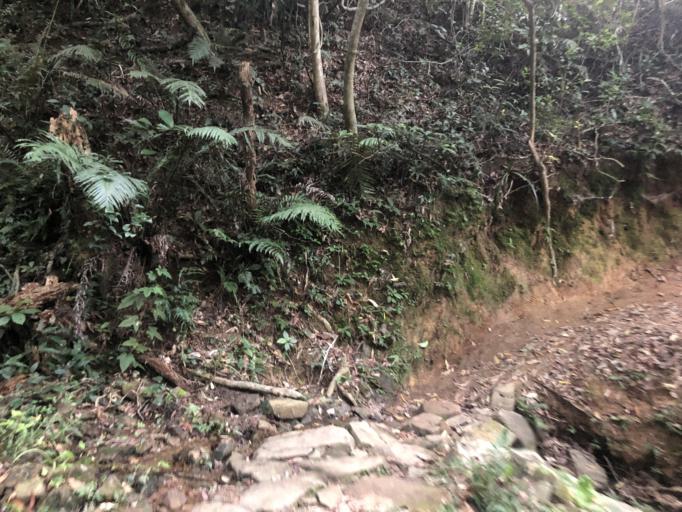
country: HK
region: Tsuen Wan
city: Tsuen Wan
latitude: 22.3991
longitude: 114.0786
